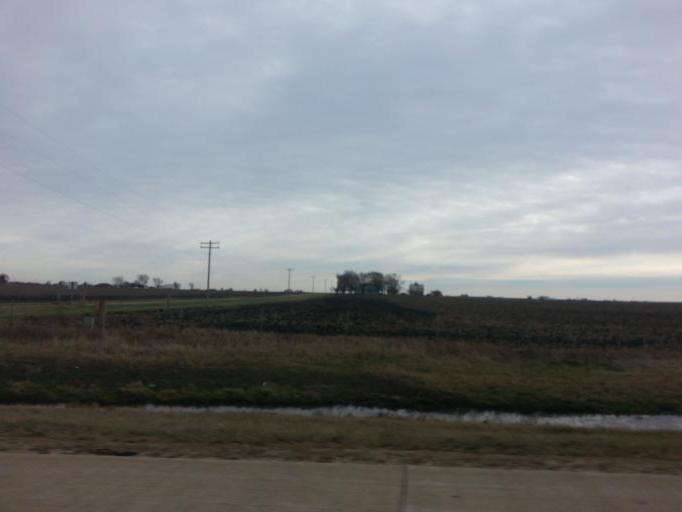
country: US
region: Illinois
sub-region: Woodford County
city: El Paso
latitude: 40.7221
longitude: -89.0340
